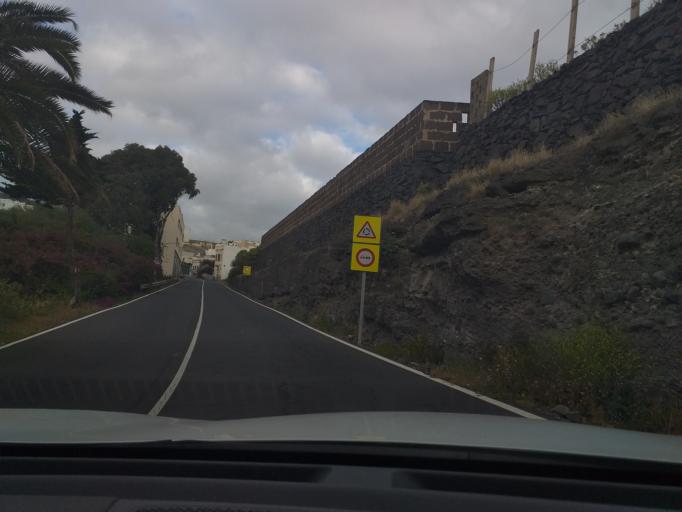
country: ES
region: Canary Islands
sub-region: Provincia de Las Palmas
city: Arucas
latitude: 28.1080
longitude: -15.5037
